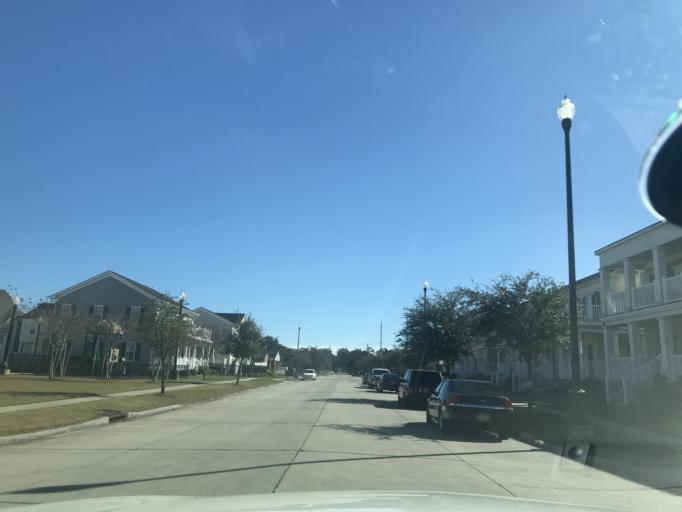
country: US
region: Louisiana
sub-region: Orleans Parish
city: New Orleans
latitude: 29.9520
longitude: -90.0950
